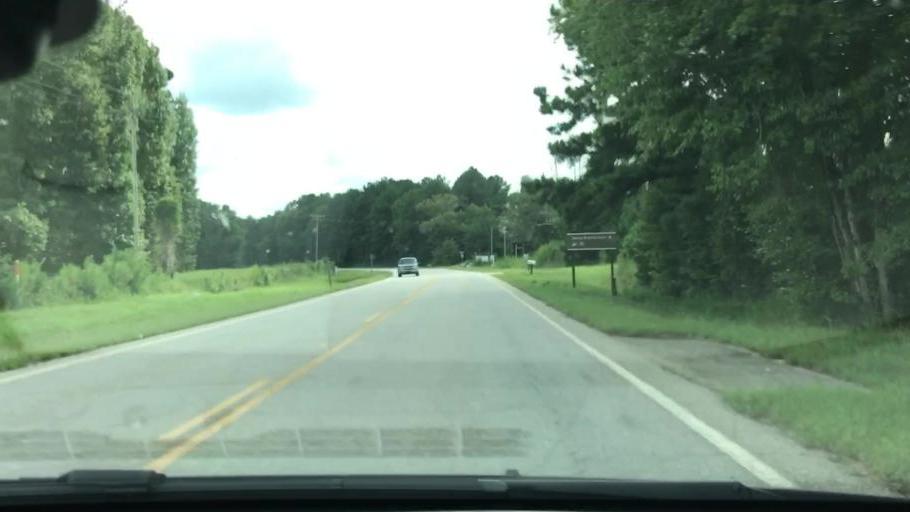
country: US
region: Georgia
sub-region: Clay County
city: Fort Gaines
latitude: 31.6944
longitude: -85.0457
